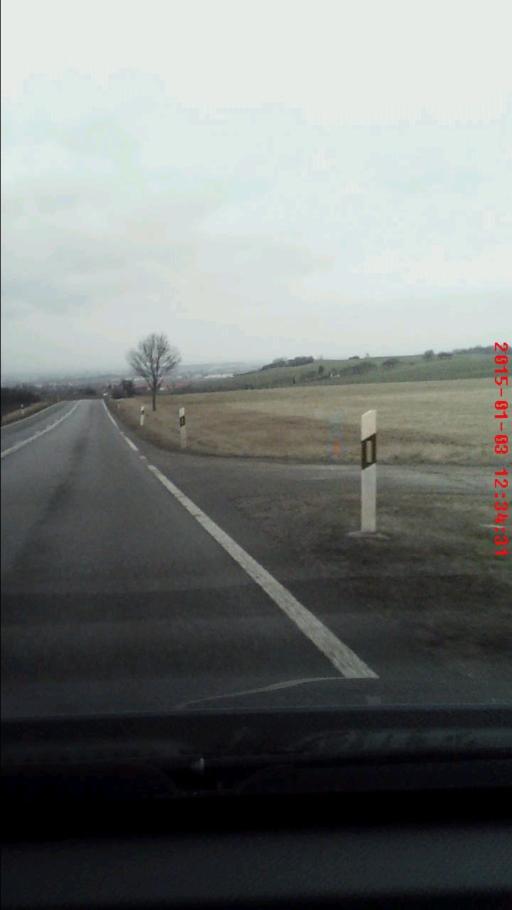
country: DE
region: Thuringia
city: Klettbach
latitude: 50.9368
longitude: 11.1220
